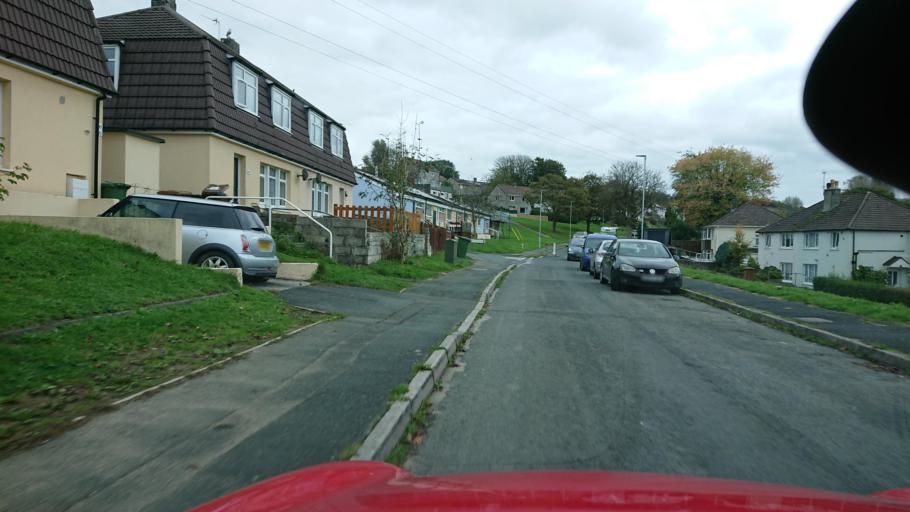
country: GB
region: England
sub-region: Plymouth
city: Plymouth
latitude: 50.4148
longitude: -4.1460
